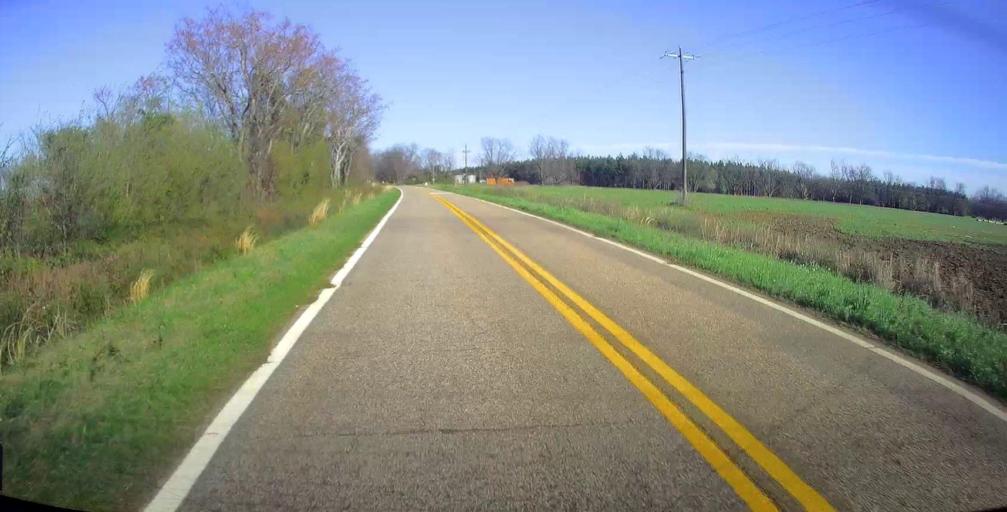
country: US
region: Georgia
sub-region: Peach County
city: Byron
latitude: 32.6580
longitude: -83.8633
